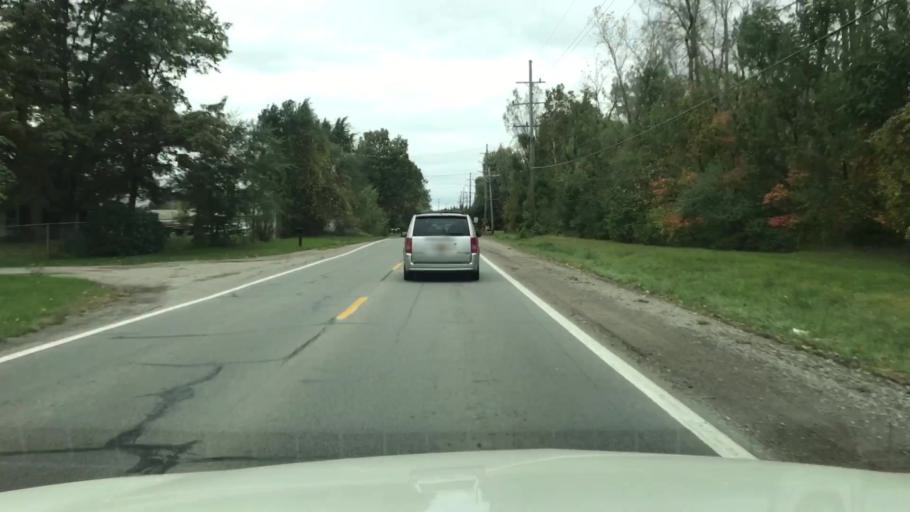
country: US
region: Michigan
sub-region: Macomb County
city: Shelby
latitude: 42.6631
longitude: -83.0735
